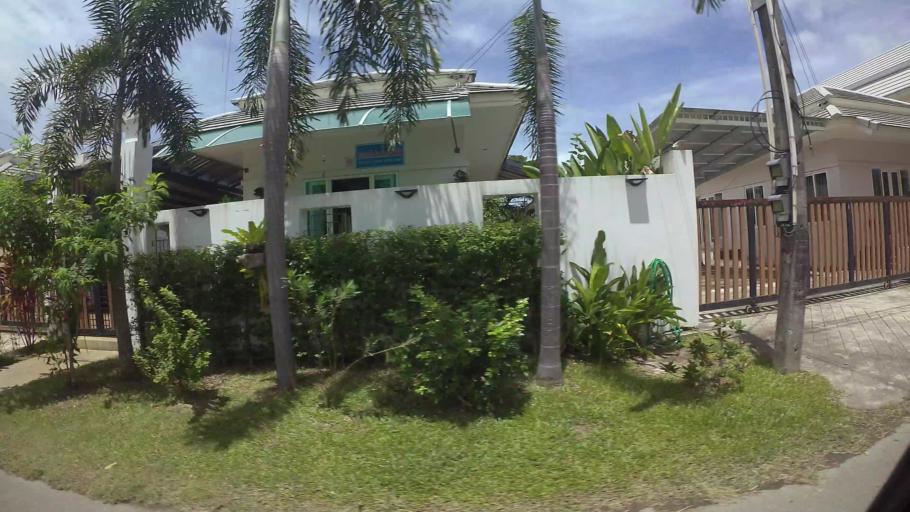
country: TH
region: Chon Buri
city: Sattahip
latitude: 12.7423
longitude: 100.8908
